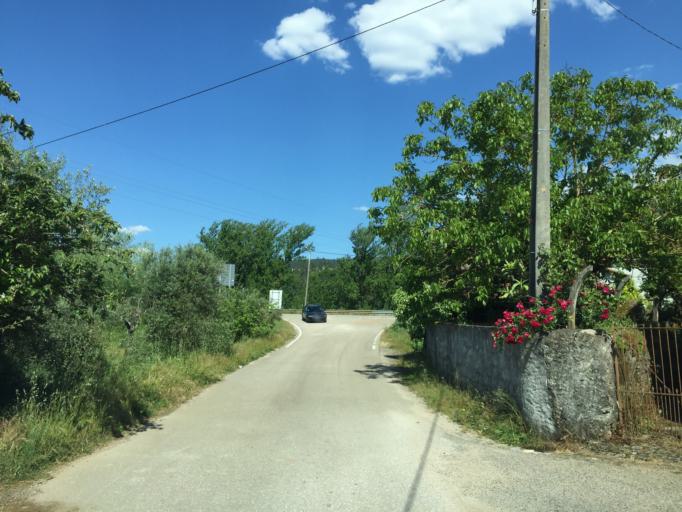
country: PT
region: Leiria
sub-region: Alvaiazere
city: Alvaiazere
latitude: 39.8472
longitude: -8.3486
